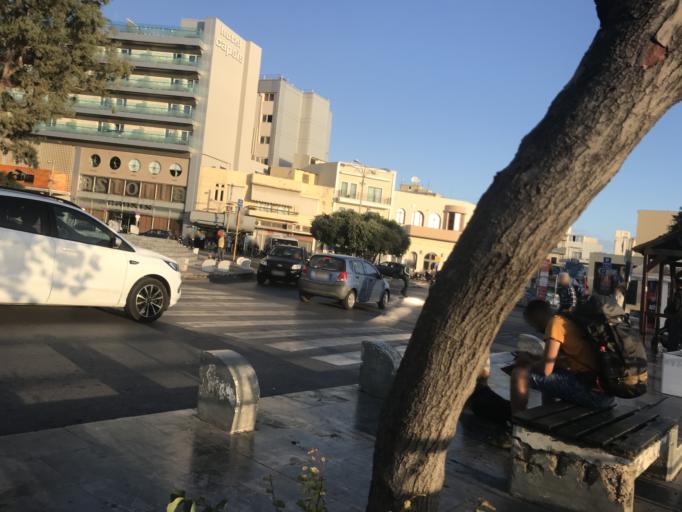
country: GR
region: Crete
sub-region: Nomos Irakleiou
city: Irakleion
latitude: 35.3380
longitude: 25.1370
